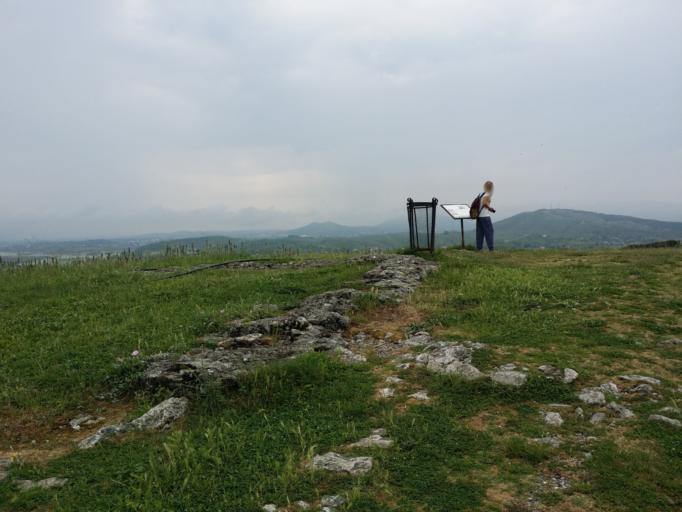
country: AL
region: Shkoder
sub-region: Rrethi i Shkodres
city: Shkoder
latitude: 42.0466
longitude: 19.4936
